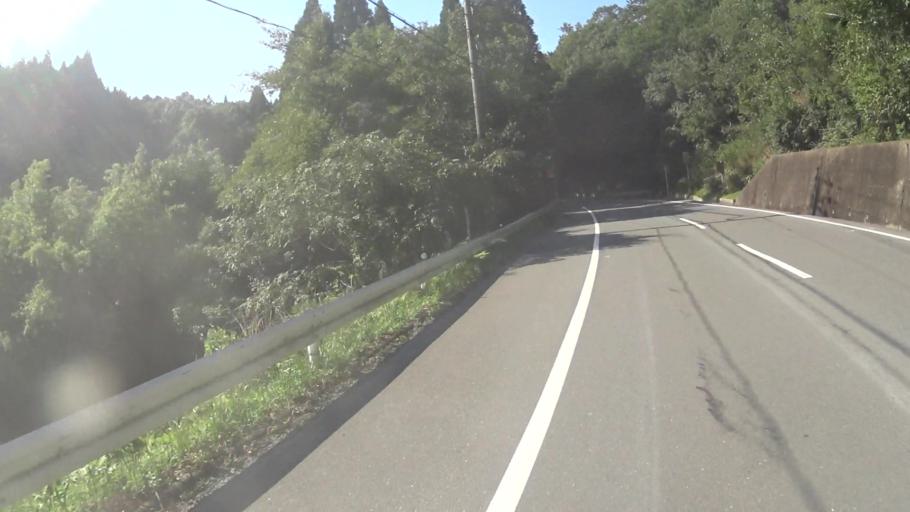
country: JP
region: Kyoto
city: Kameoka
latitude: 34.9626
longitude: 135.5322
